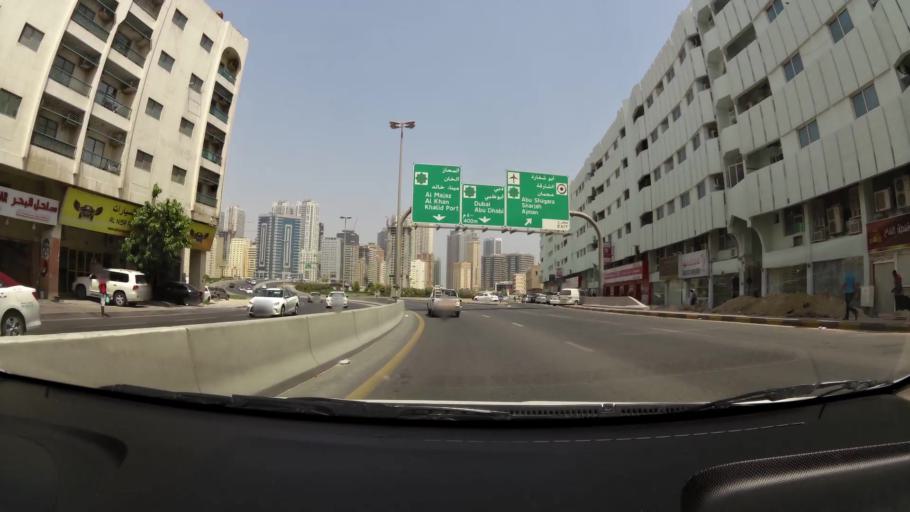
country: AE
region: Ash Shariqah
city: Sharjah
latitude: 25.3126
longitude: 55.3845
